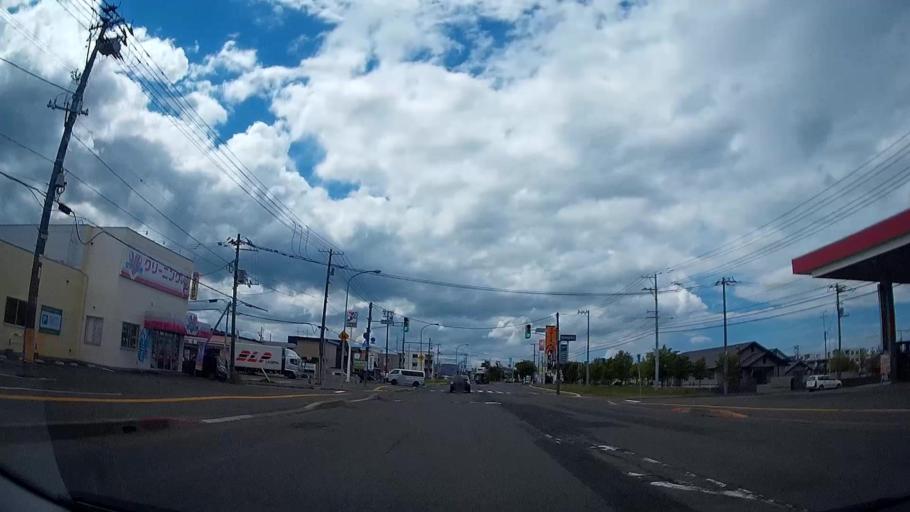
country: JP
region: Hokkaido
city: Chitose
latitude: 42.8713
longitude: 141.5870
